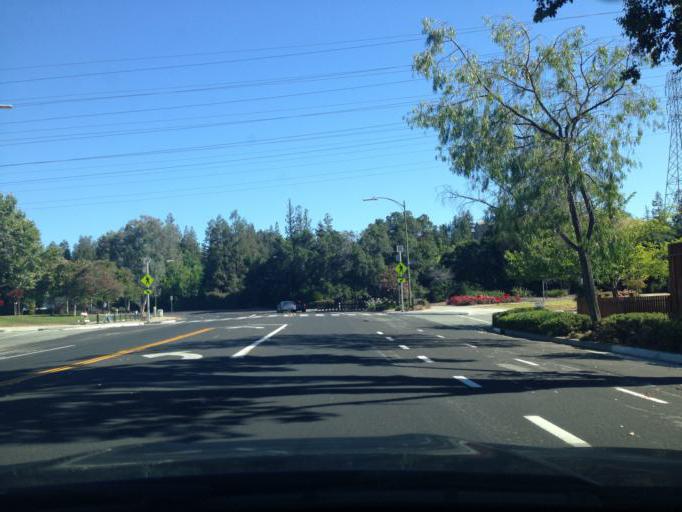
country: US
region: California
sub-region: Santa Clara County
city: Cambrian Park
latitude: 37.2318
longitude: -121.8840
